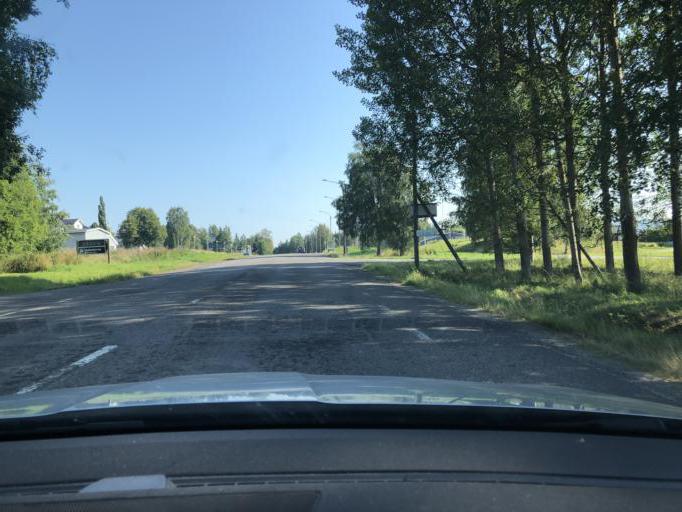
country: SE
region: Vaesternorrland
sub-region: Kramfors Kommun
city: Kramfors
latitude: 62.8766
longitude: 17.8619
